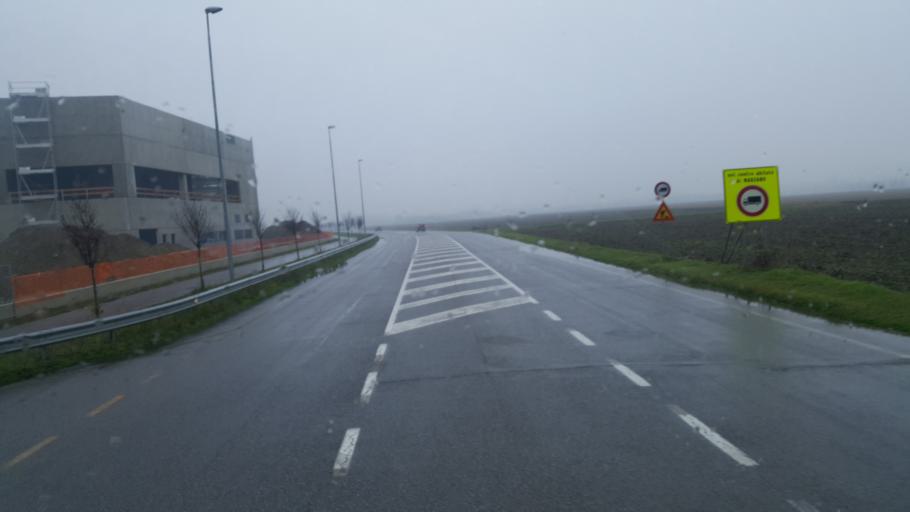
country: IT
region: Lombardy
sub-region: Provincia di Pavia
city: Marzano
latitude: 45.2612
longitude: 9.2972
